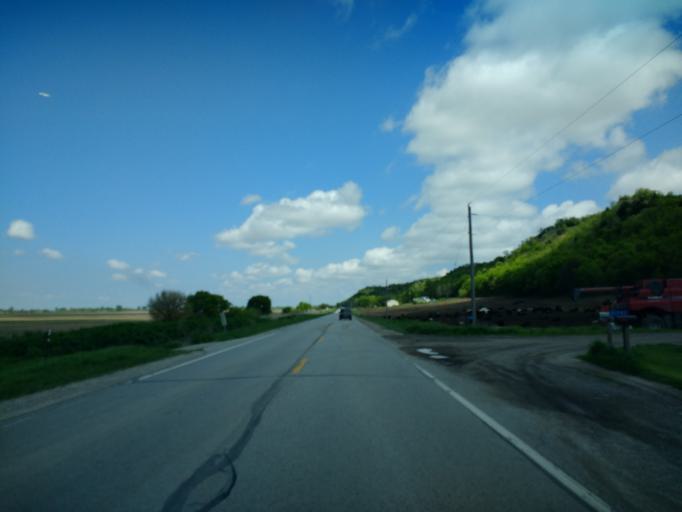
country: US
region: Iowa
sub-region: Harrison County
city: Missouri Valley
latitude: 41.4715
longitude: -95.8806
